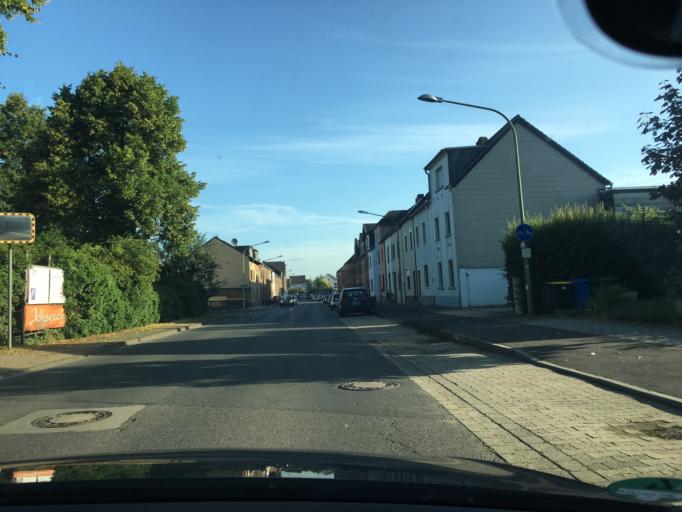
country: DE
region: North Rhine-Westphalia
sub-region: Regierungsbezirk Koln
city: Dueren
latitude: 50.8345
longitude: 6.4906
